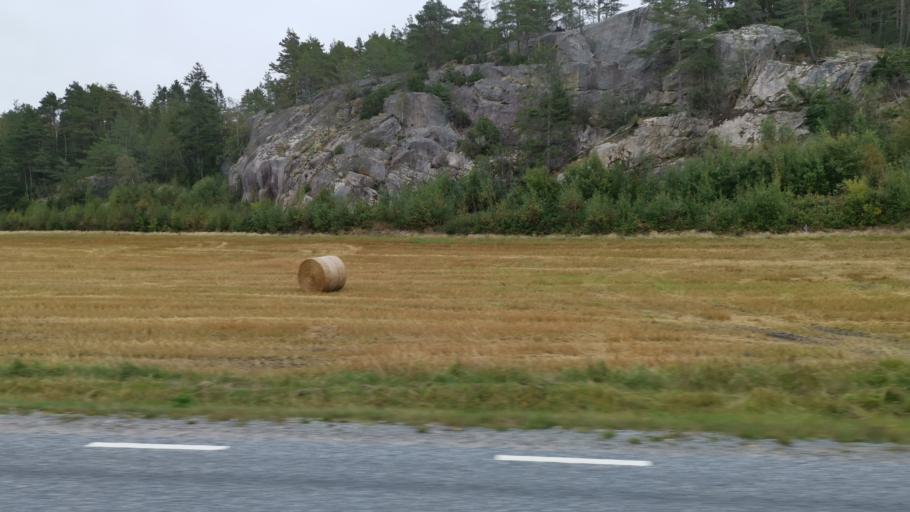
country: SE
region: Vaestra Goetaland
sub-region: Tanums Kommun
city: Tanumshede
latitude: 58.6765
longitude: 11.3405
